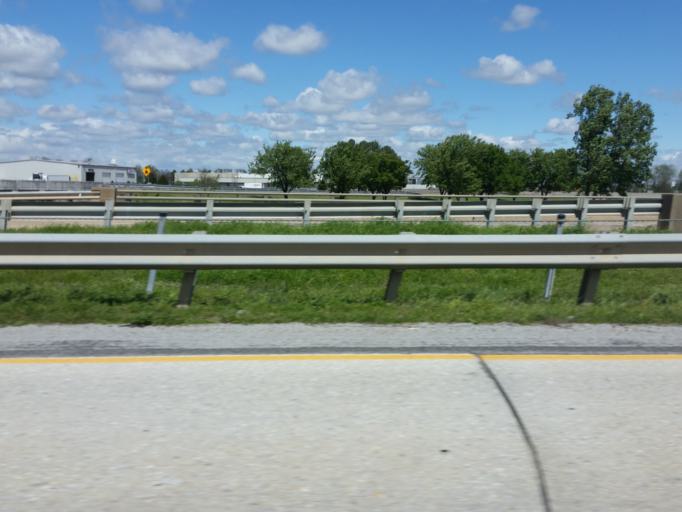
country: US
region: Arkansas
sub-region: Craighead County
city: Jonesboro
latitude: 35.8068
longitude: -90.6404
